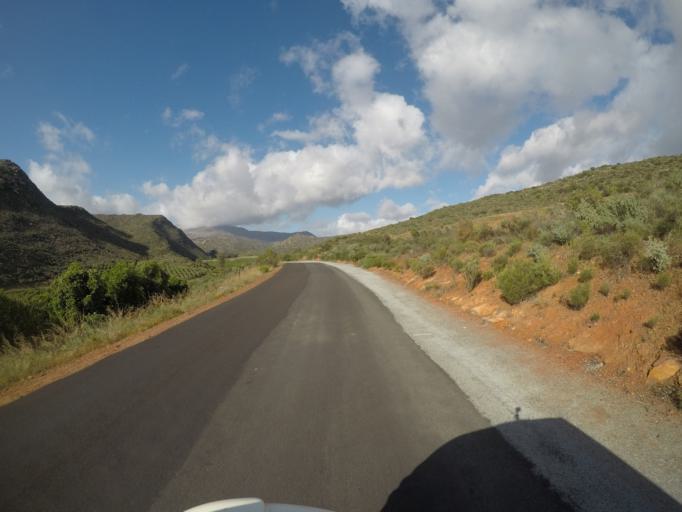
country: ZA
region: Western Cape
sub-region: West Coast District Municipality
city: Clanwilliam
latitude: -32.4345
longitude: 18.9467
